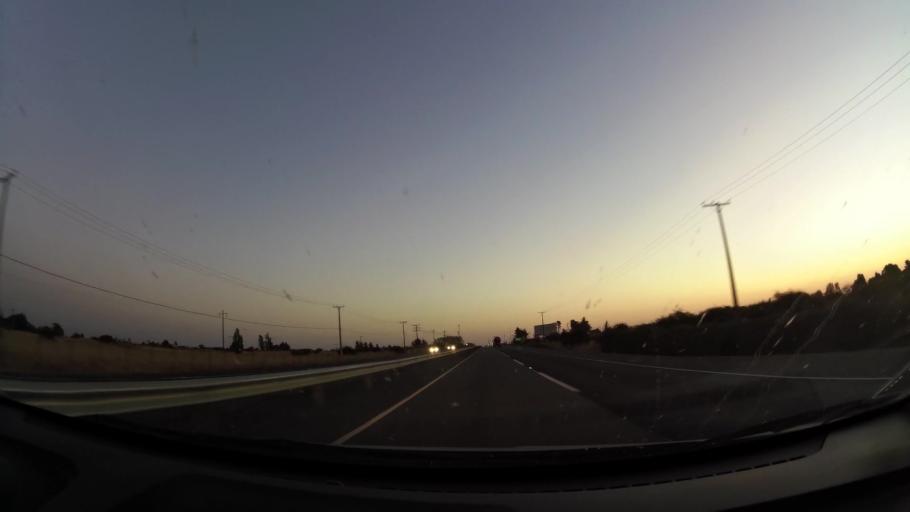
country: CL
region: Maule
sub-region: Provincia de Linares
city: Parral
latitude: -36.1205
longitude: -71.8036
